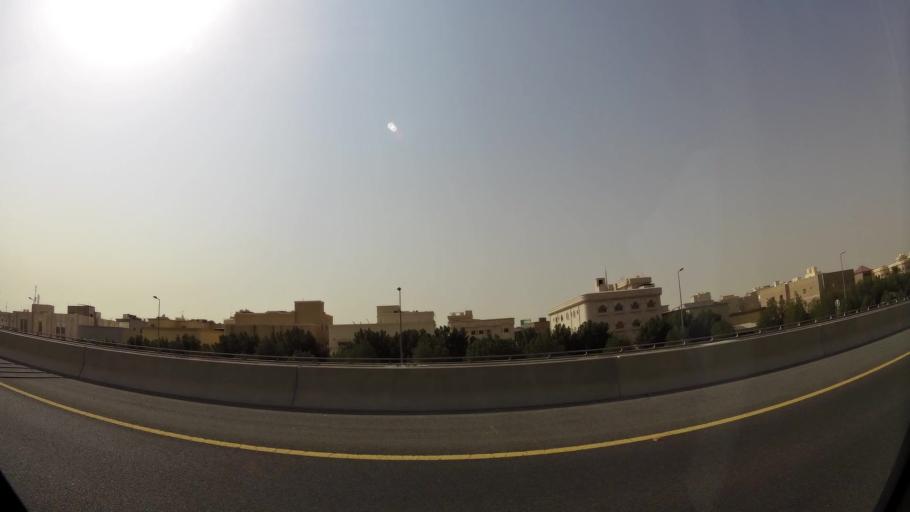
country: KW
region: Muhafazat al Jahra'
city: Al Jahra'
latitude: 29.3541
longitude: 47.6840
